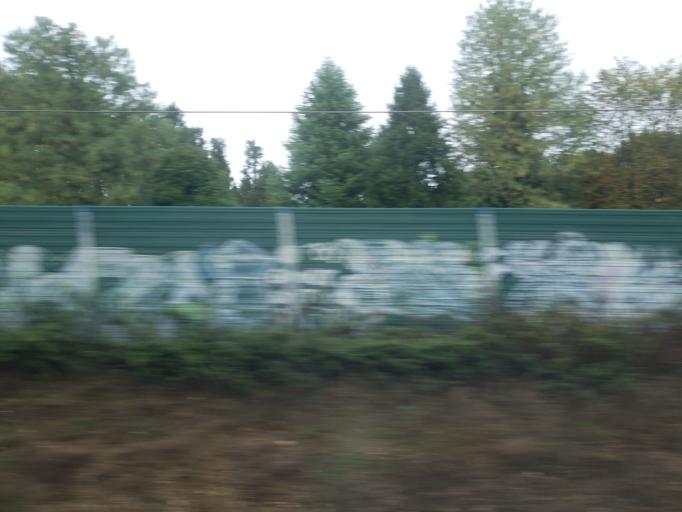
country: IT
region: Lombardy
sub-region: Provincia di Varese
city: Cascina Elisa
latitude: 45.6000
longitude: 8.8006
